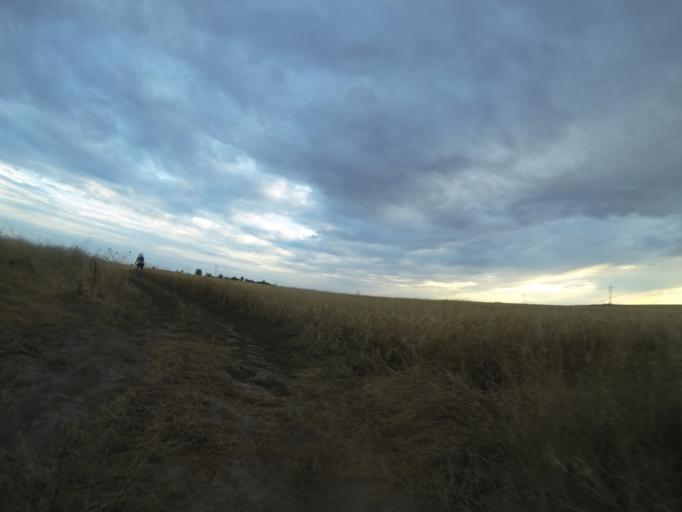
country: RO
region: Dolj
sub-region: Comuna Almaju
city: Almaju
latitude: 44.4677
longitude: 23.7116
